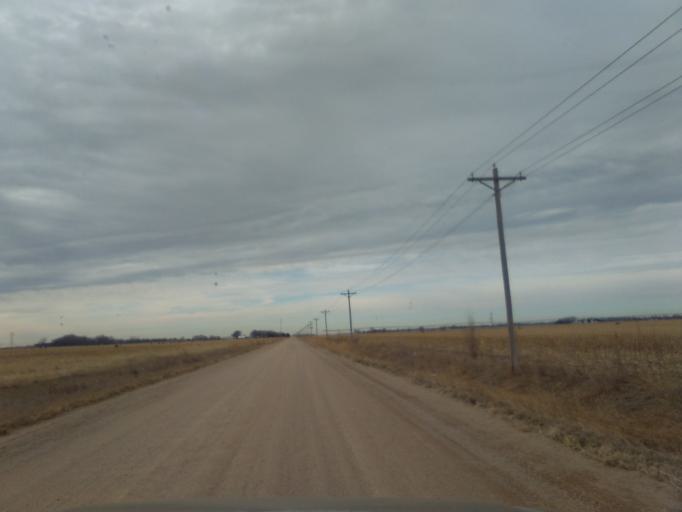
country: US
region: Nebraska
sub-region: Buffalo County
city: Gibbon
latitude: 40.6406
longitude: -98.8768
